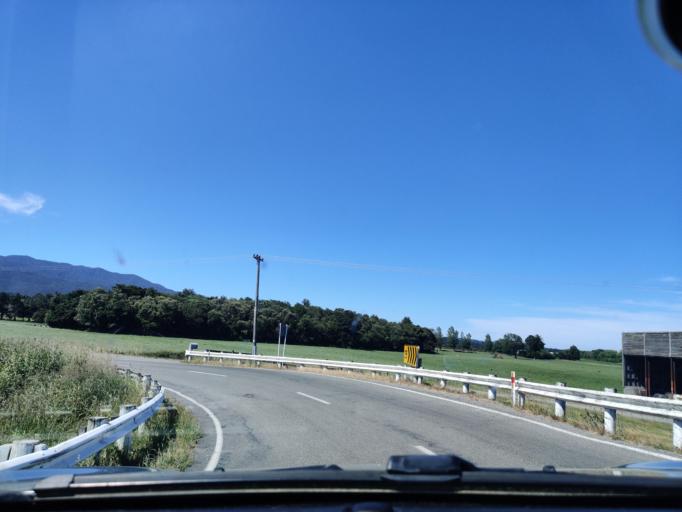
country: NZ
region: Wellington
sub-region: Upper Hutt City
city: Upper Hutt
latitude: -41.2873
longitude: 175.2682
